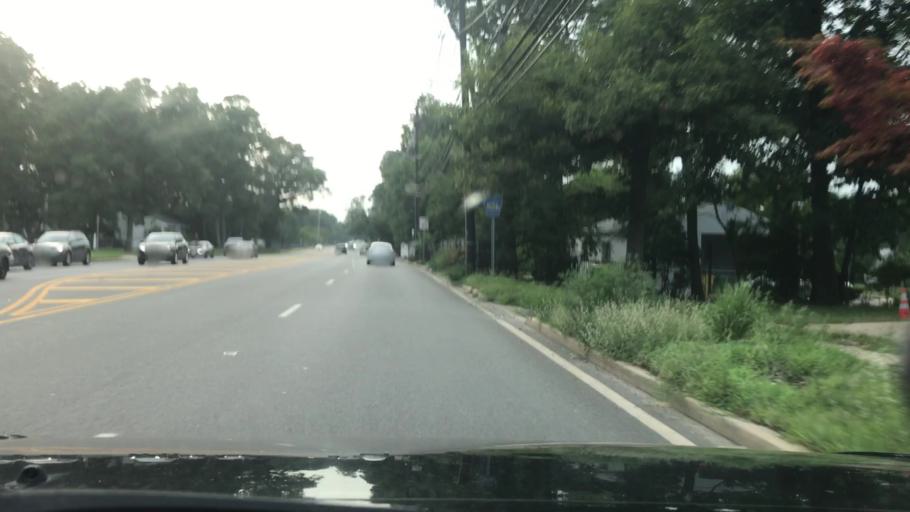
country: US
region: New Jersey
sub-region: Ocean County
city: Lakewood
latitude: 40.1110
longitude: -74.2395
